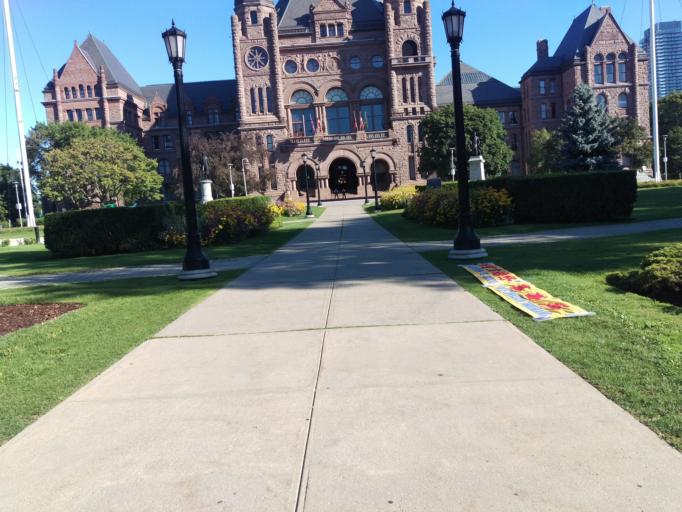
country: CA
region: Ontario
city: Toronto
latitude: 43.6611
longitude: -79.3910
